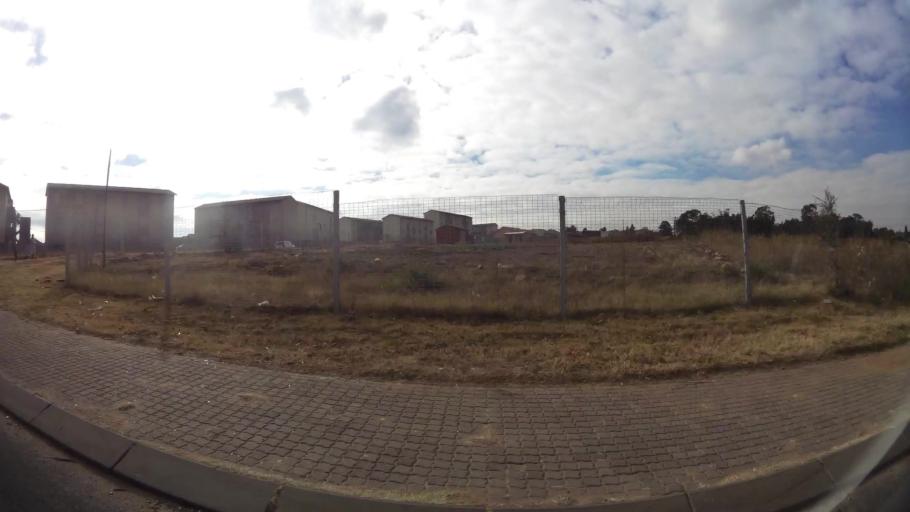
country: ZA
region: Gauteng
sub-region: City of Johannesburg Metropolitan Municipality
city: Roodepoort
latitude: -26.1949
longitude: 27.9103
